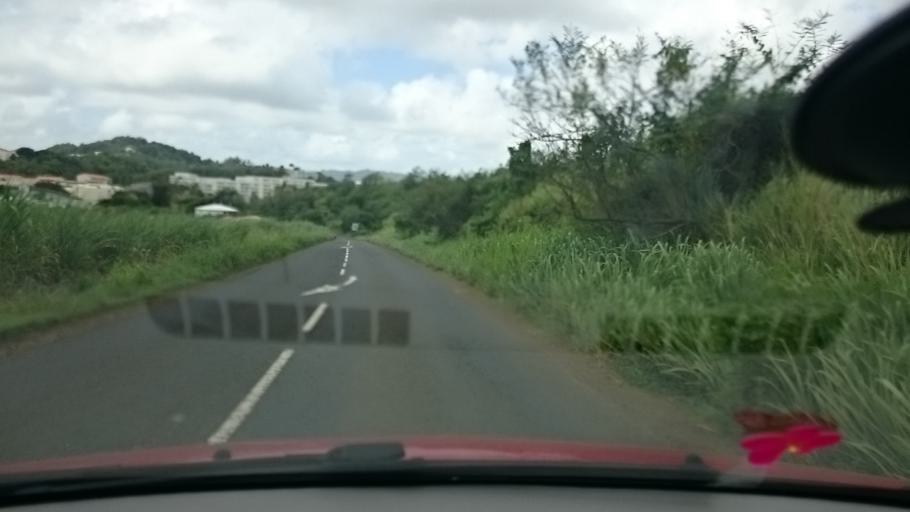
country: MQ
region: Martinique
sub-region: Martinique
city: La Trinite
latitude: 14.7495
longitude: -60.9452
